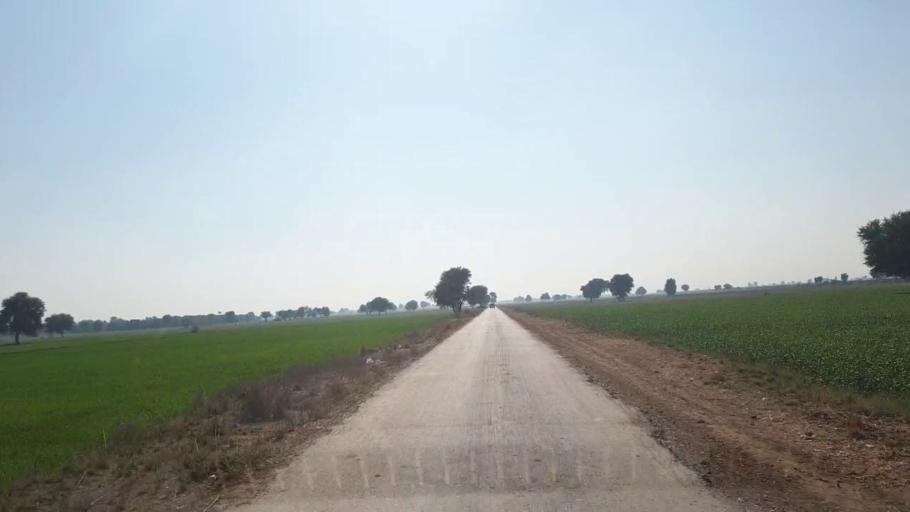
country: PK
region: Sindh
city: Shahpur Chakar
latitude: 26.1123
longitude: 68.6288
